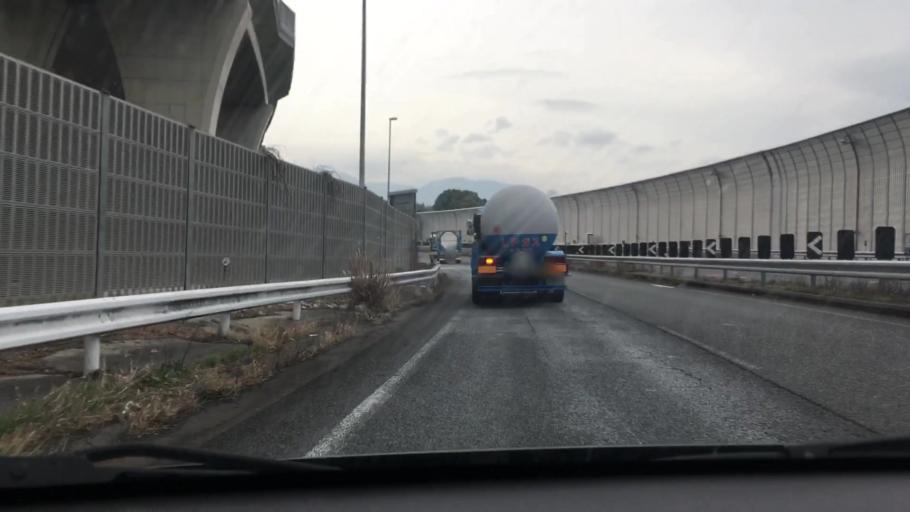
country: JP
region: Mie
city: Kameyama
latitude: 34.8519
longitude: 136.4172
